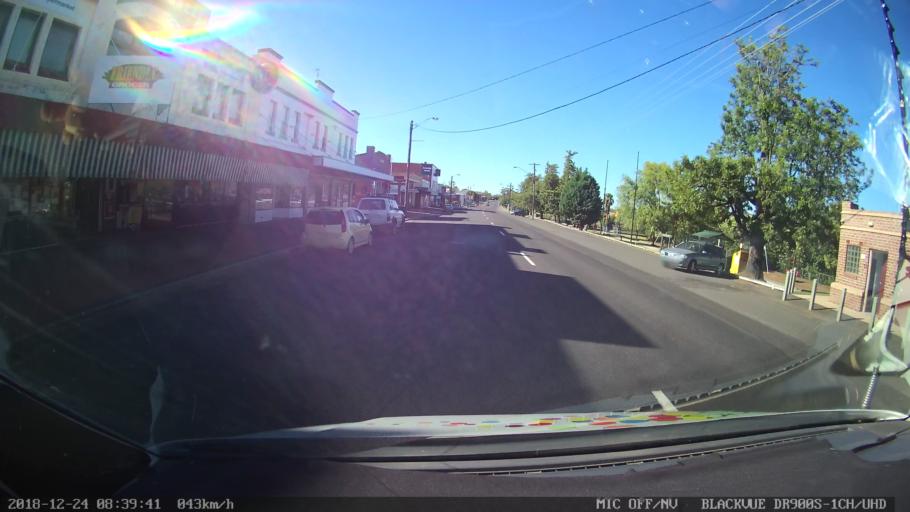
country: AU
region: New South Wales
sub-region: Liverpool Plains
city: Quirindi
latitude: -31.3498
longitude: 150.6472
